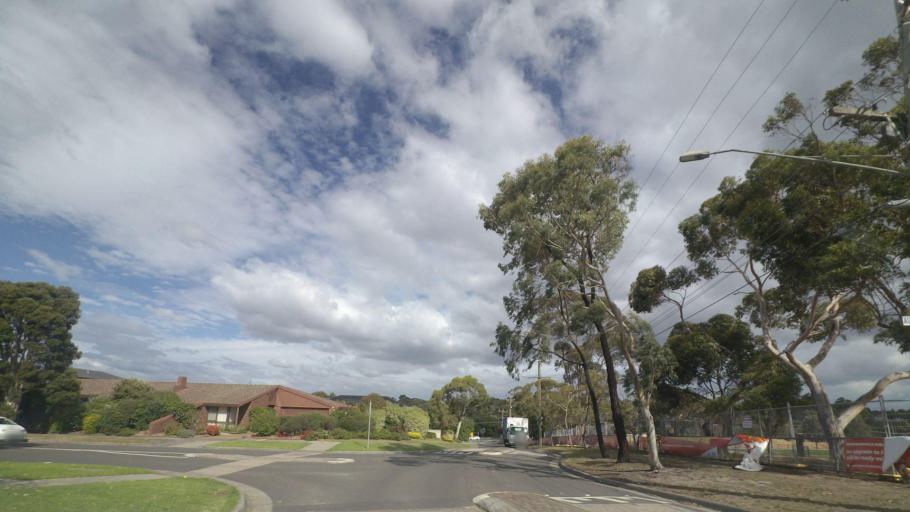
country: AU
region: Victoria
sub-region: Nillumbik
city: Eltham
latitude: -37.7604
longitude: 145.1534
